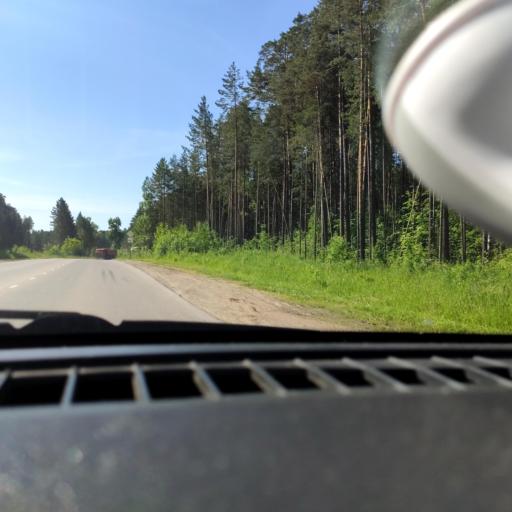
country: RU
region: Perm
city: Overyata
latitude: 57.9993
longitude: 55.8801
